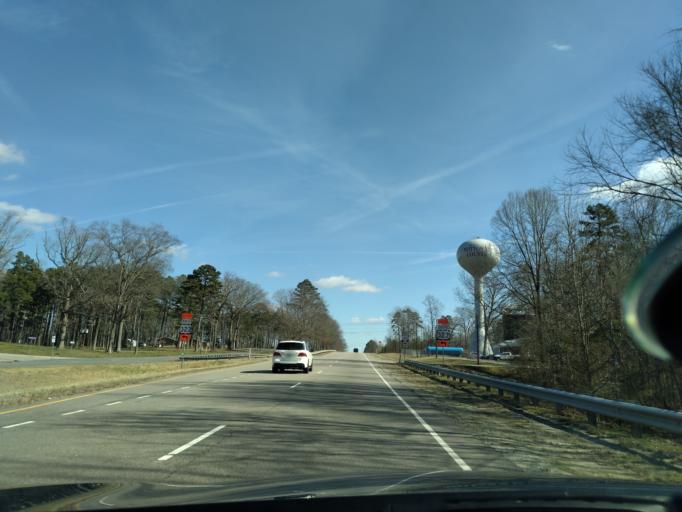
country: US
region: Virginia
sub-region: Nottoway County
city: Crewe
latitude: 37.1896
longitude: -78.1746
